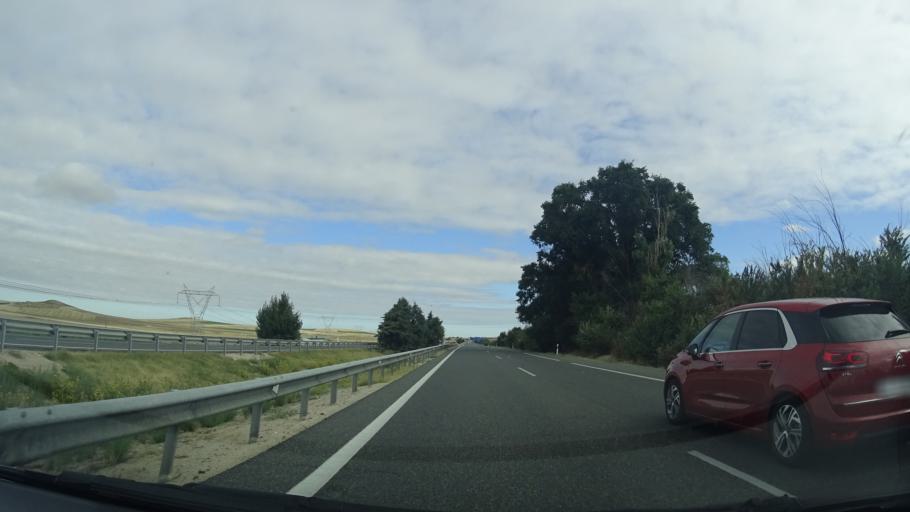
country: ES
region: Castille and Leon
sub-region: Provincia de Valladolid
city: San Pablo de la Moraleja
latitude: 41.1614
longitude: -4.7974
